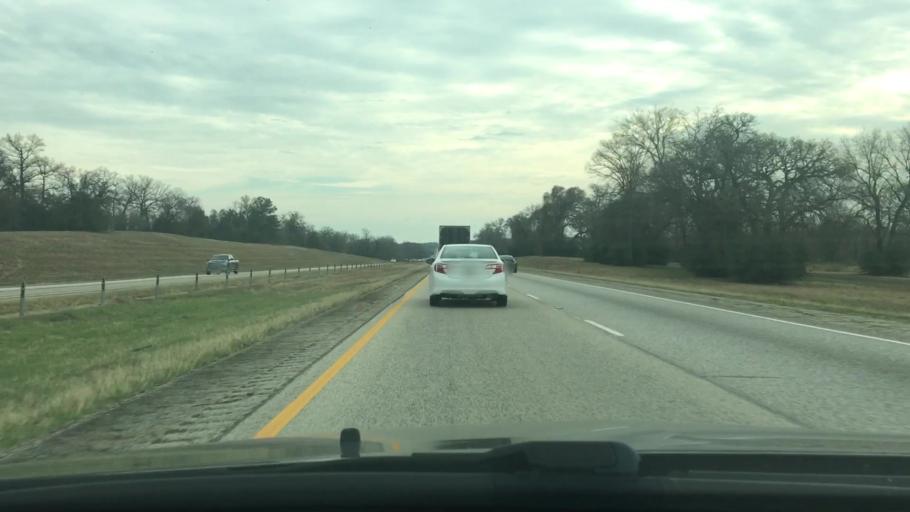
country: US
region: Texas
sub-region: Leon County
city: Centerville
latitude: 31.2041
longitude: -95.9956
